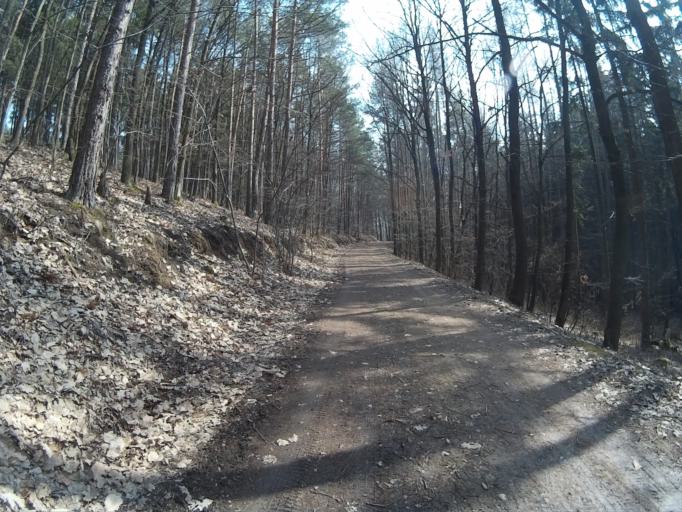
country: CZ
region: South Moravian
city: Pozorice
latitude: 49.2221
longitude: 16.7921
